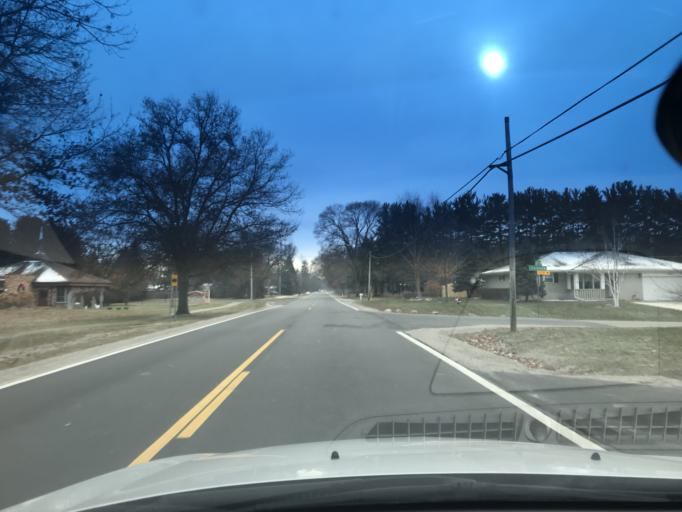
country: US
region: Michigan
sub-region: Macomb County
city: Shelby
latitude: 42.6661
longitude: -83.0617
